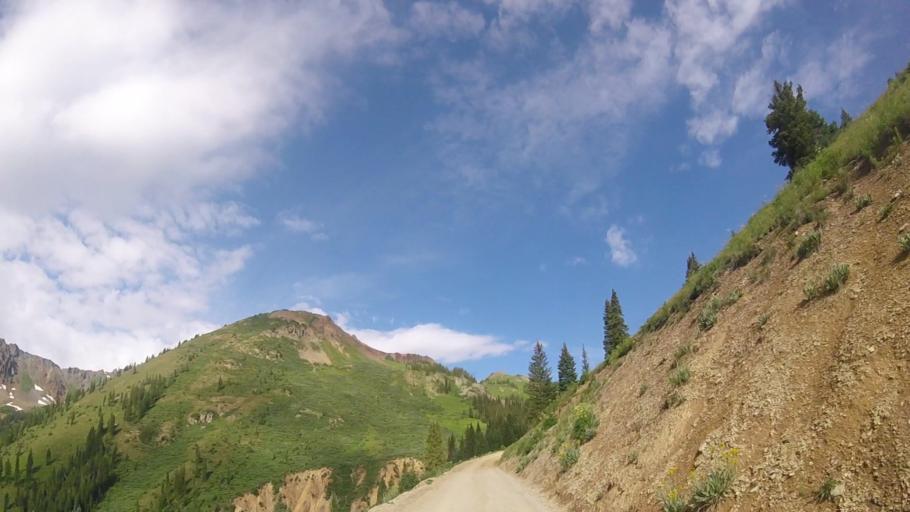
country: US
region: Colorado
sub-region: San Miguel County
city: Telluride
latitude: 37.8458
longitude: -107.7659
